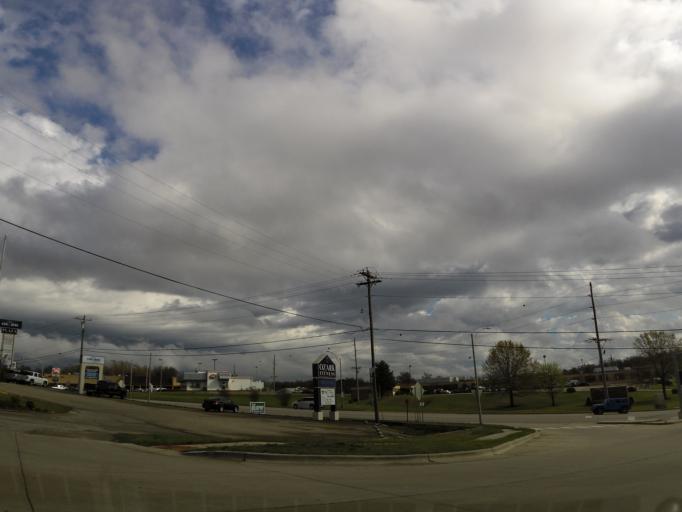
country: US
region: Missouri
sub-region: Butler County
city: Poplar Bluff
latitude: 36.7840
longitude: -90.4288
